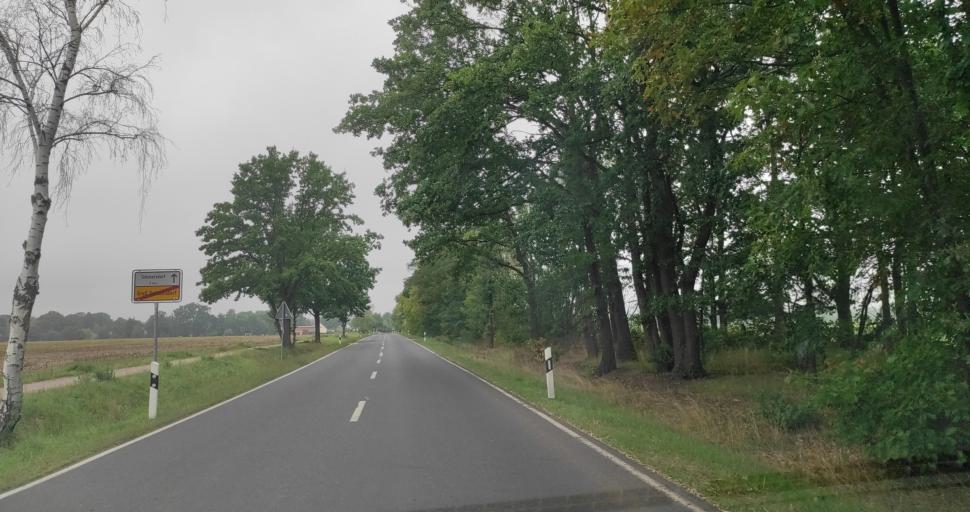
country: DE
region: Brandenburg
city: Forst
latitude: 51.6889
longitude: 14.6195
